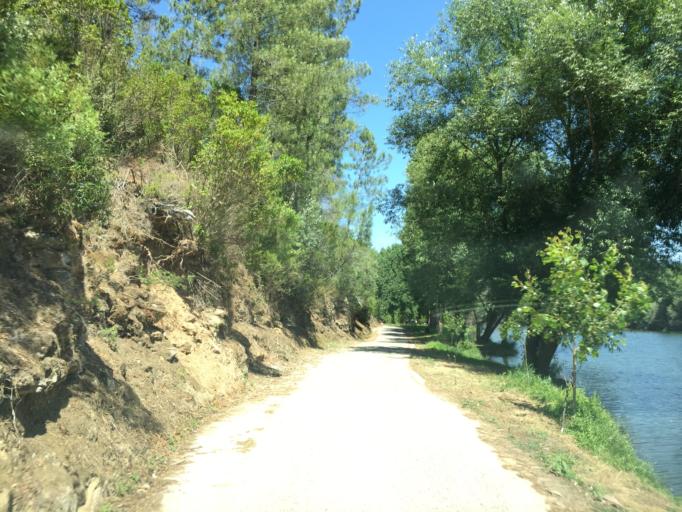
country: PT
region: Coimbra
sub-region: Pampilhosa da Serra
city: Pampilhosa da Serra
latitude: 40.0102
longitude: -7.8449
